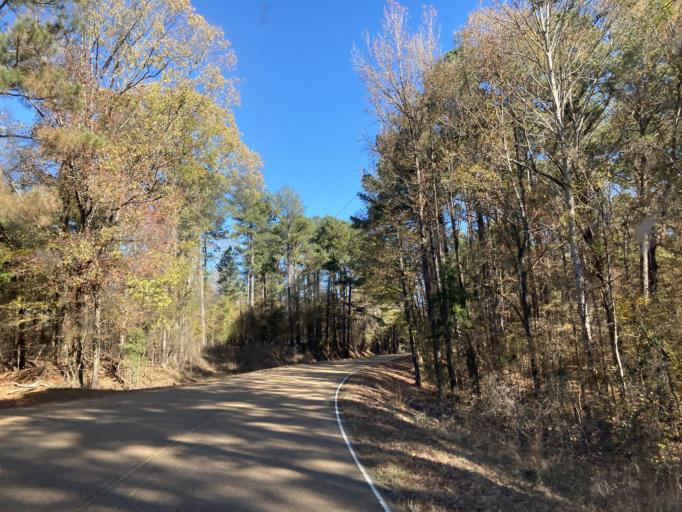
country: US
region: Mississippi
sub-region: Hinds County
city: Lynchburg
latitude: 32.6218
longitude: -90.5240
